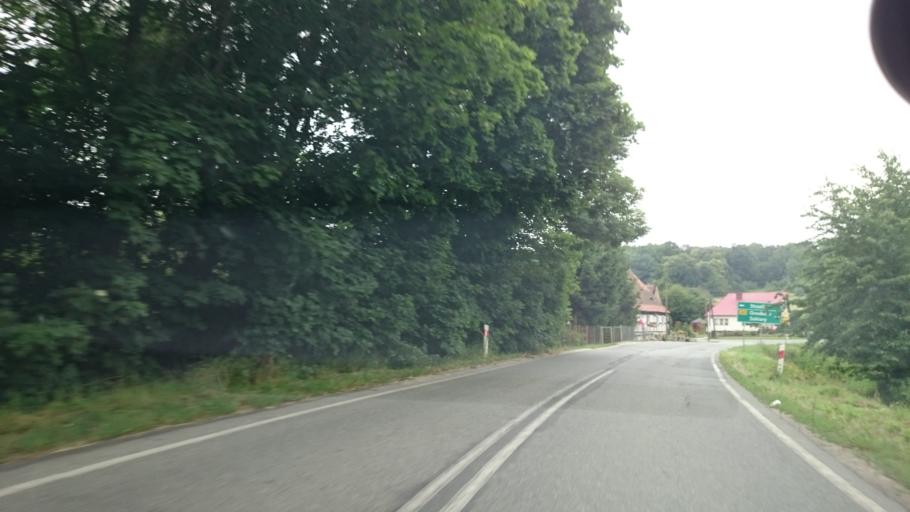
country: PL
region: Lower Silesian Voivodeship
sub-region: Powiat strzelinski
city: Przeworno
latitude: 50.6478
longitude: 17.1700
